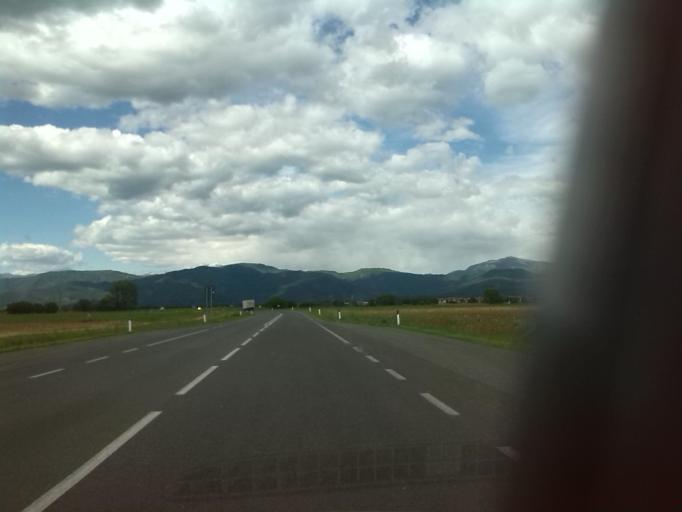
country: IT
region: Friuli Venezia Giulia
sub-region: Provincia di Udine
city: Orsaria
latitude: 46.0525
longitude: 13.3795
